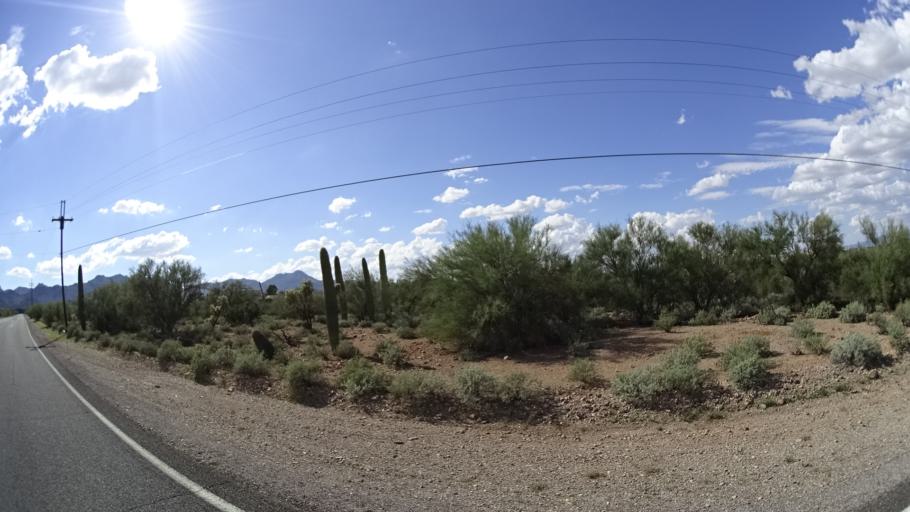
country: US
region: Arizona
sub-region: Pima County
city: Flowing Wells
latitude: 32.2774
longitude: -111.0573
